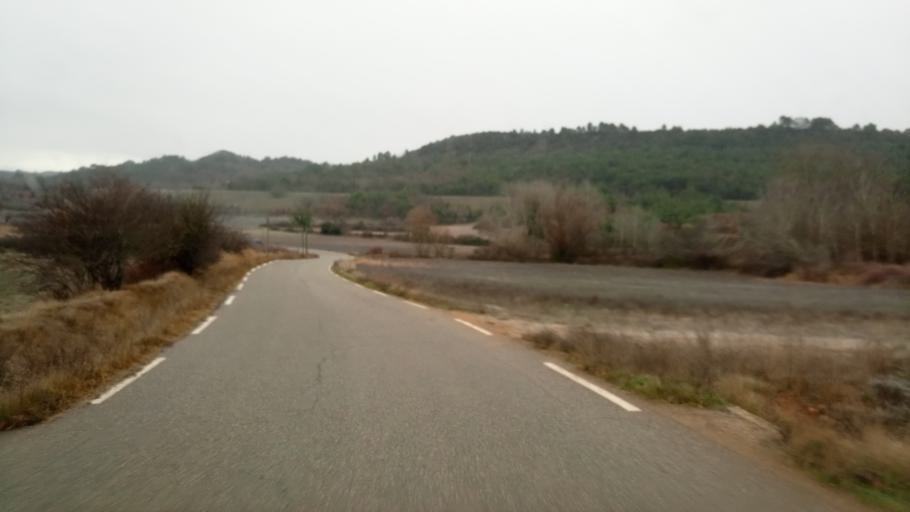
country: FR
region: Provence-Alpes-Cote d'Azur
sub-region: Departement du Var
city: Ginasservis
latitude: 43.7126
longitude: 5.8569
